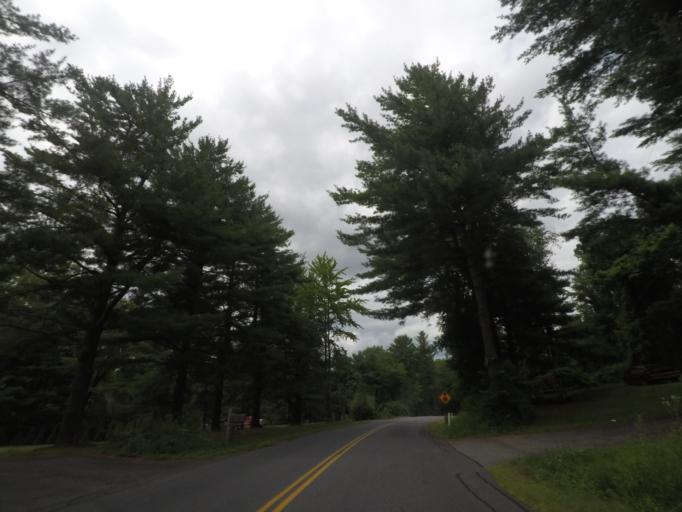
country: US
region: New York
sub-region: Saratoga County
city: Stillwater
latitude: 43.0018
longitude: -73.6957
